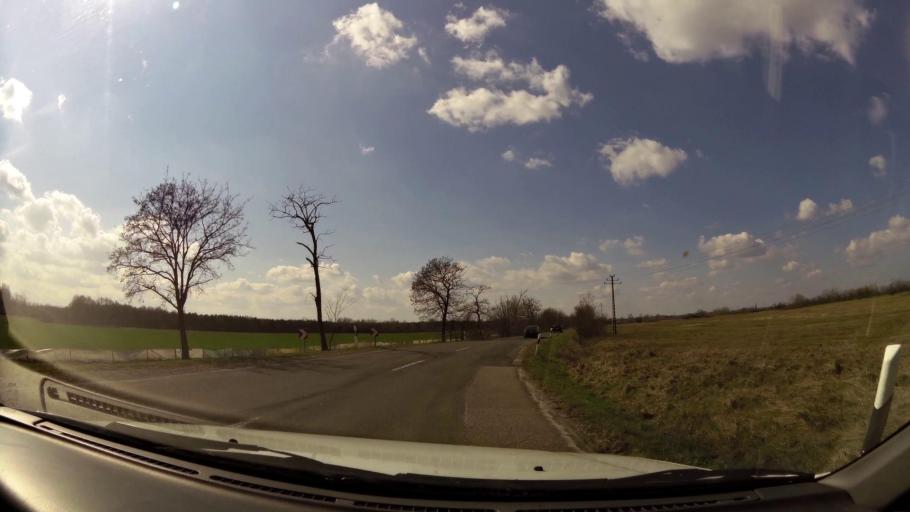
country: HU
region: Pest
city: Farmos
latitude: 47.3549
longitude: 19.8314
